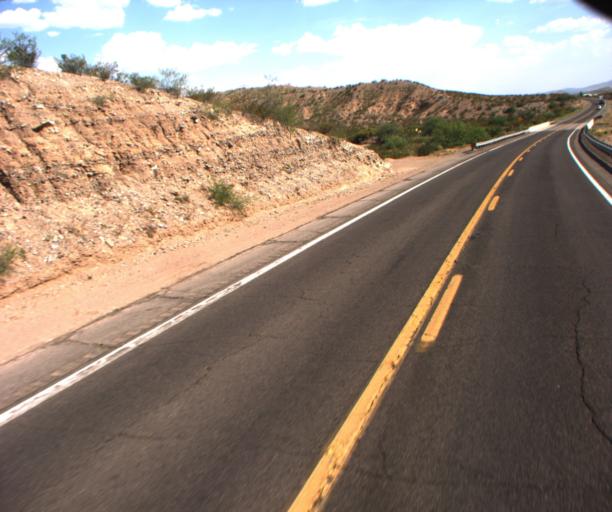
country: US
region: Arizona
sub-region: Greenlee County
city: Clifton
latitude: 32.8088
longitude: -109.1677
